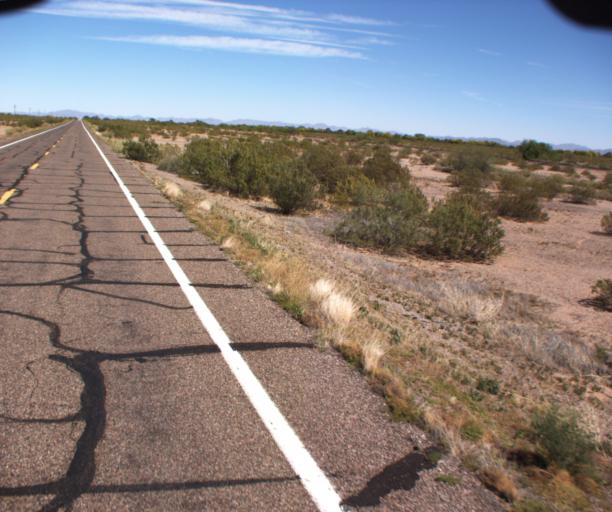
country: US
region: Arizona
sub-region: Maricopa County
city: Gila Bend
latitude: 32.8233
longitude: -112.7866
